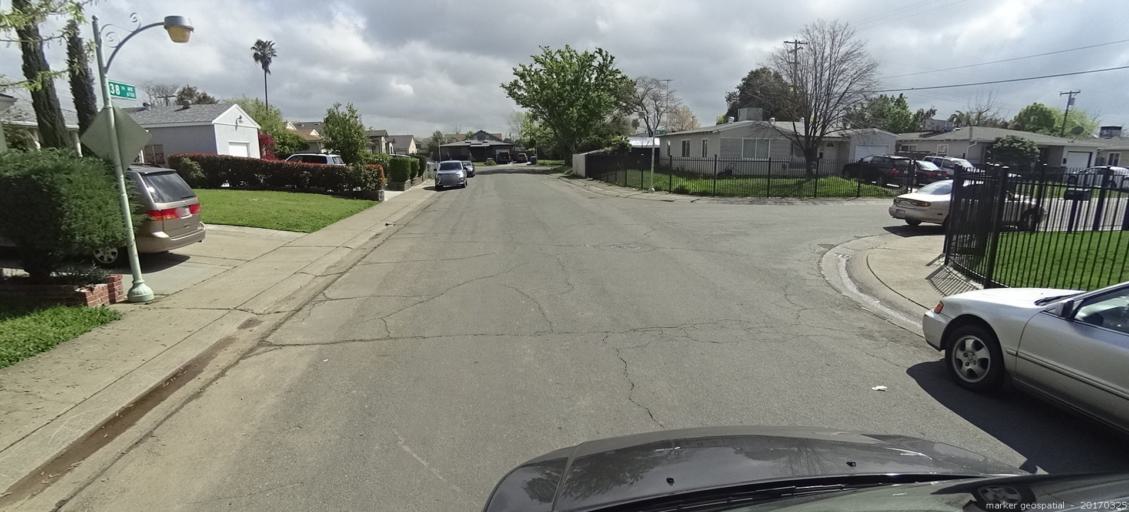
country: US
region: California
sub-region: Sacramento County
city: Florin
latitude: 38.5204
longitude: -121.4244
